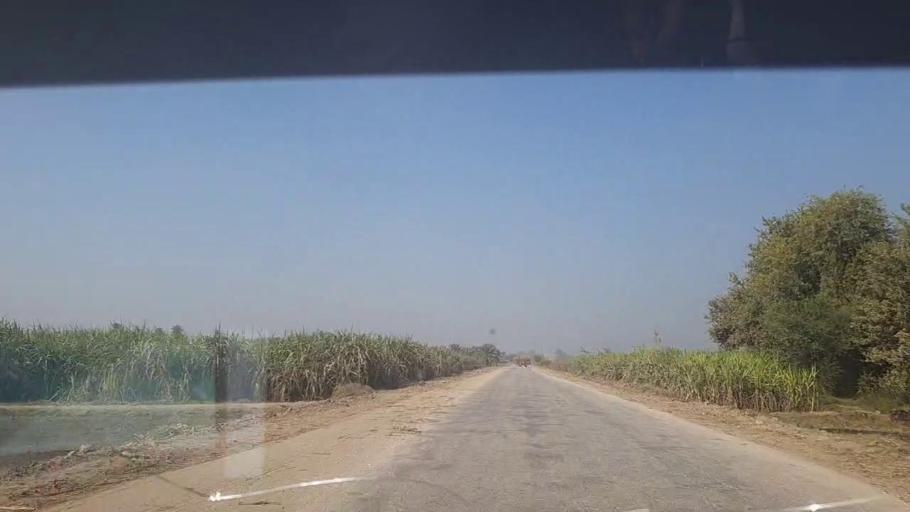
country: PK
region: Sindh
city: Kot Diji
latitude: 27.4224
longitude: 68.6593
